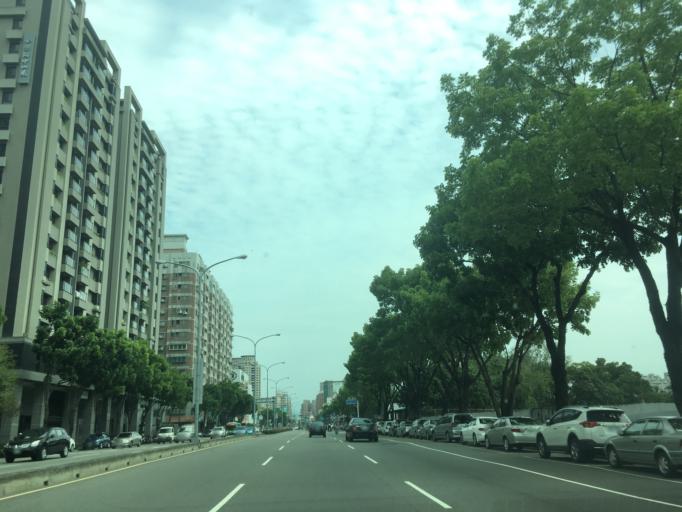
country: TW
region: Taiwan
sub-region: Taichung City
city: Taichung
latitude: 24.1200
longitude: 120.6507
